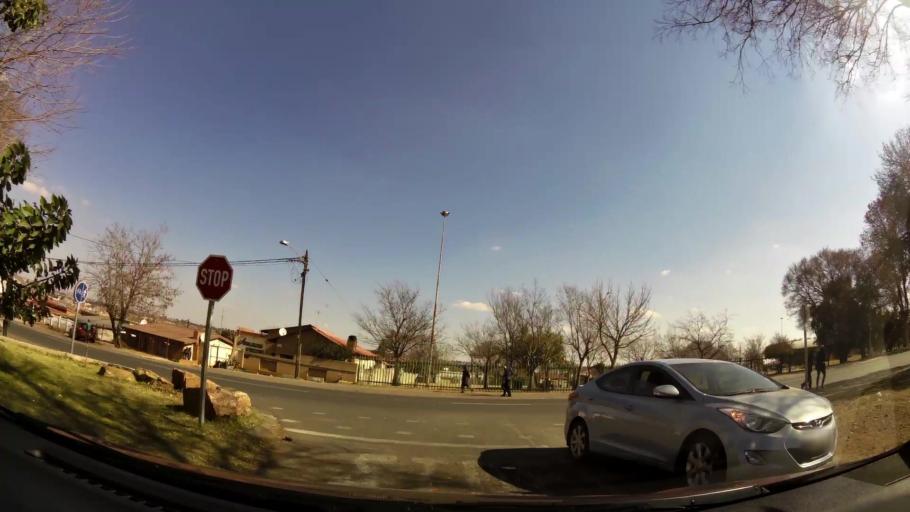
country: ZA
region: Gauteng
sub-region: City of Johannesburg Metropolitan Municipality
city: Soweto
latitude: -26.2400
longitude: 27.8946
